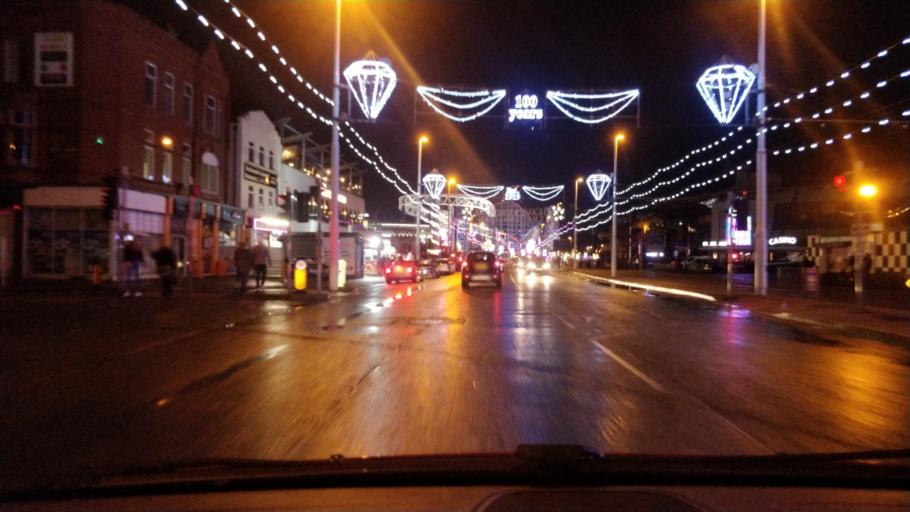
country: GB
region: England
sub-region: Blackpool
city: Blackpool
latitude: 53.7962
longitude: -3.0561
